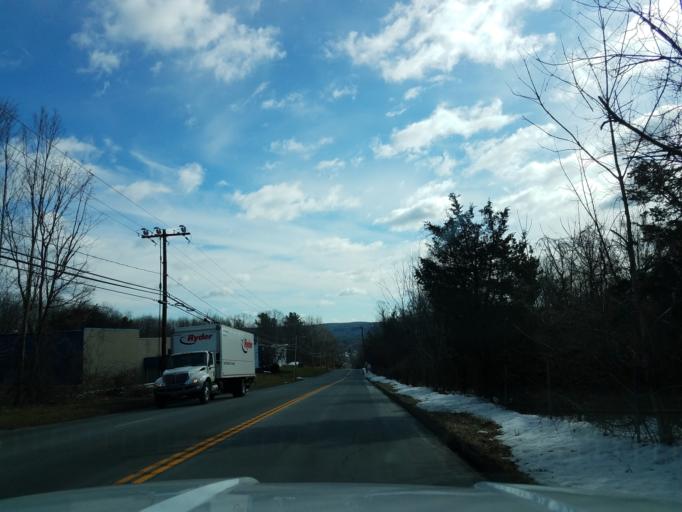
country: US
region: Connecticut
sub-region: Hartford County
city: Plainville
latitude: 41.6393
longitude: -72.8909
